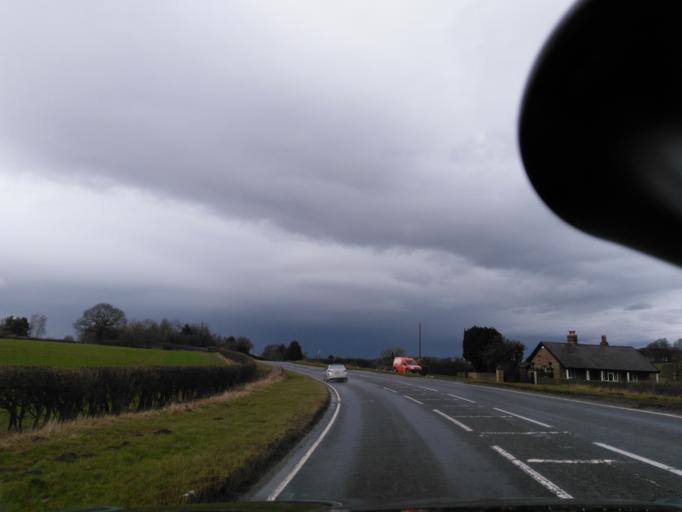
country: GB
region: England
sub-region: North Yorkshire
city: Ripon
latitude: 54.0737
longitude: -1.5357
